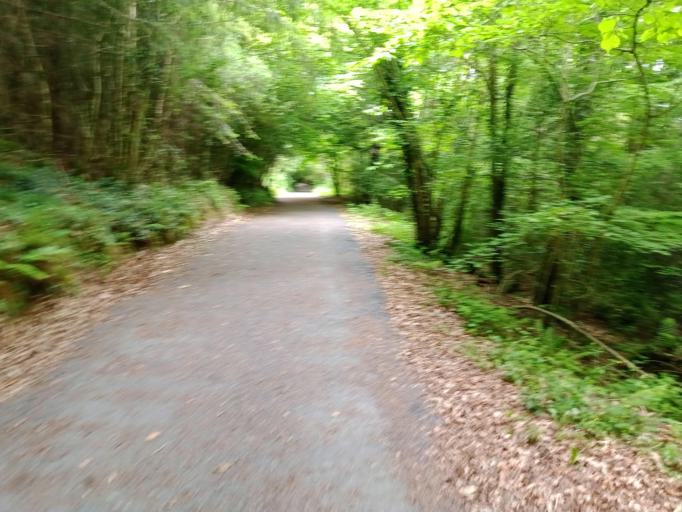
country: IE
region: Leinster
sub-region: Kilkenny
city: Thomastown
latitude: 52.4706
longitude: -7.0455
